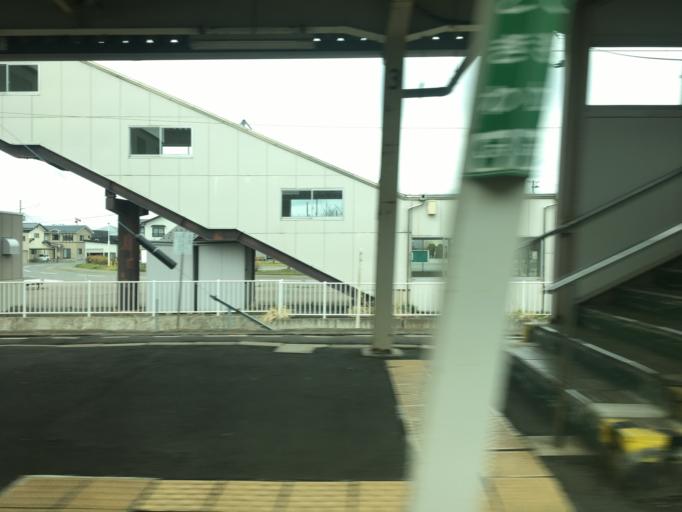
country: JP
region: Aomori
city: Kuroishi
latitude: 40.6706
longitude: 140.5436
